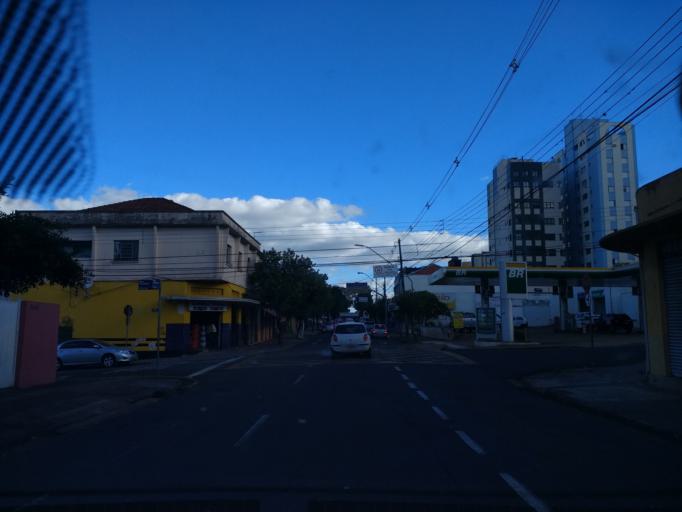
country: BR
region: Parana
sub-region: Londrina
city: Londrina
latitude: -23.3185
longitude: -51.1551
